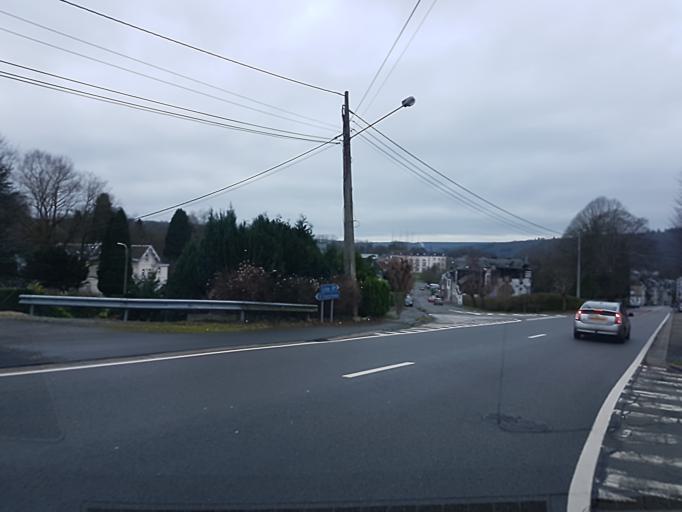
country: BE
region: Wallonia
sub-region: Province de Liege
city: Spa
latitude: 50.4883
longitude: 5.8749
